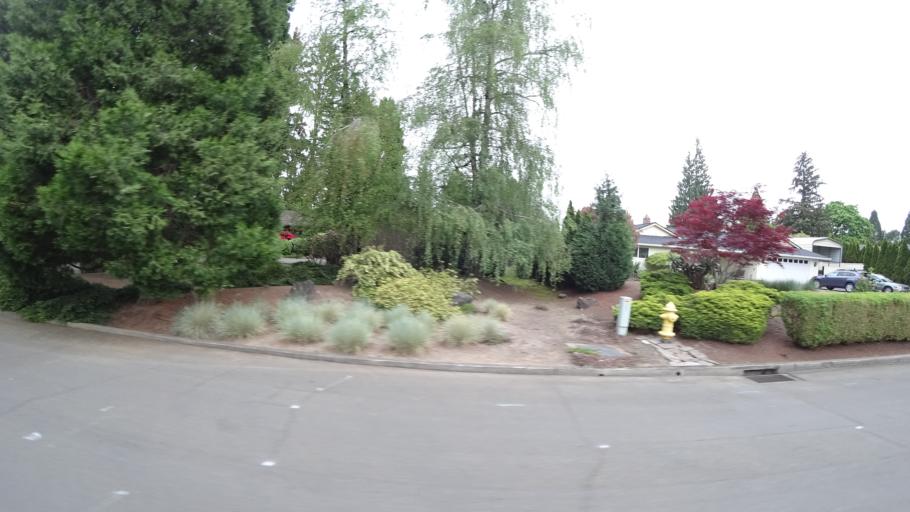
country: US
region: Oregon
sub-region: Washington County
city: Aloha
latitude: 45.5112
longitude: -122.8695
